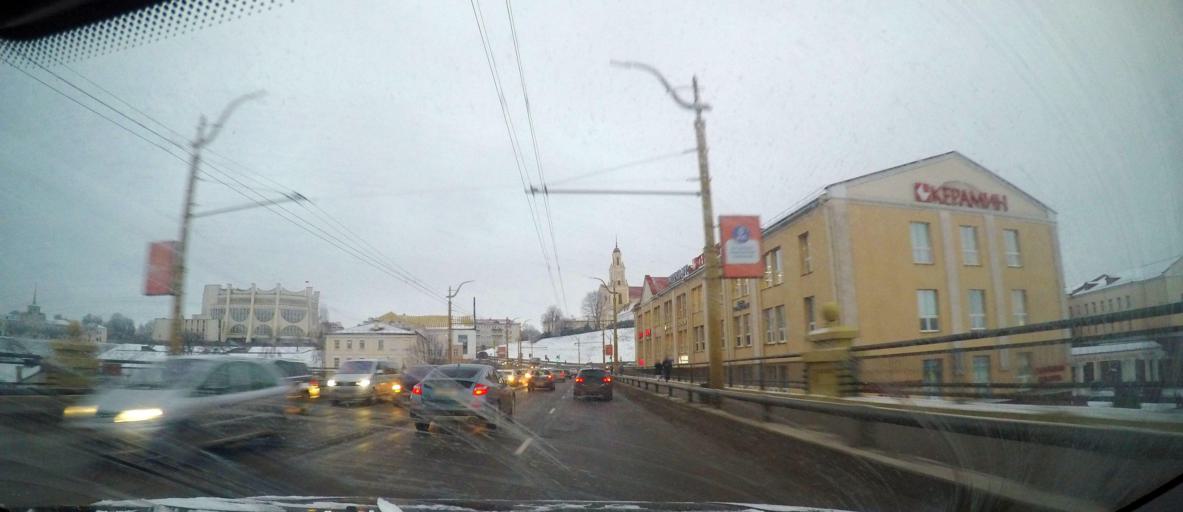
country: BY
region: Grodnenskaya
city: Hrodna
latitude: 53.6730
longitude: 23.8274
